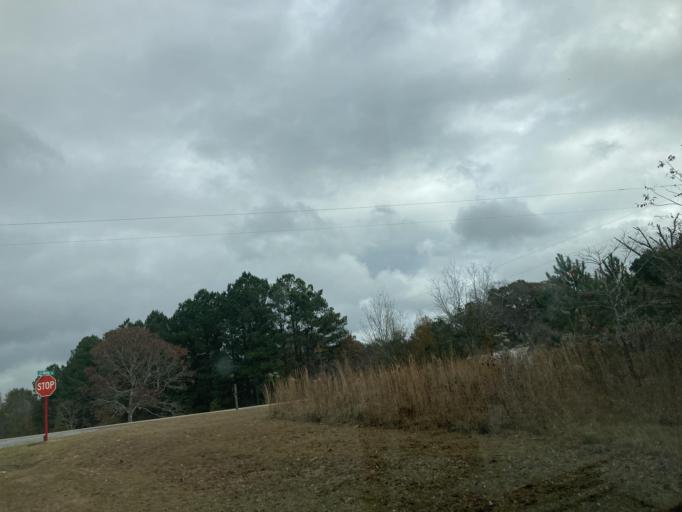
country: US
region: Mississippi
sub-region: Lamar County
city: Purvis
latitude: 31.1431
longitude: -89.5181
